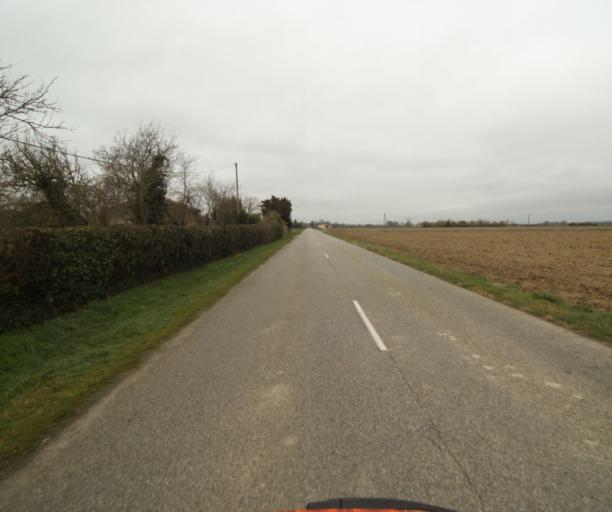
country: FR
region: Midi-Pyrenees
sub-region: Departement de l'Ariege
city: Saverdun
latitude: 43.2606
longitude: 1.5300
